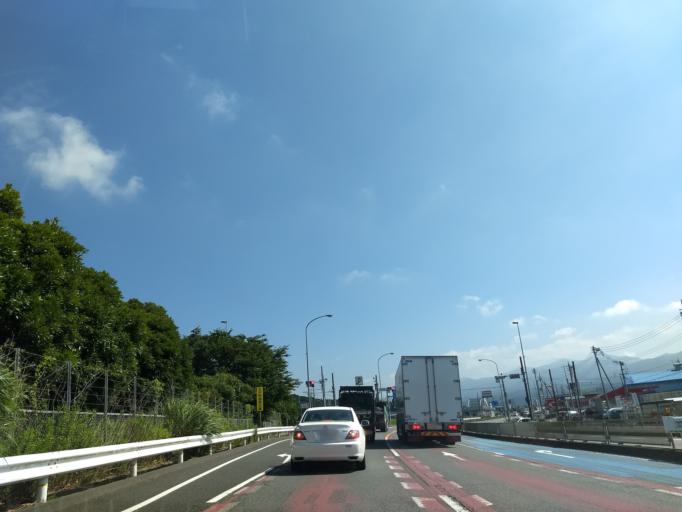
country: JP
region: Shizuoka
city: Mishima
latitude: 35.1864
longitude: 138.9022
